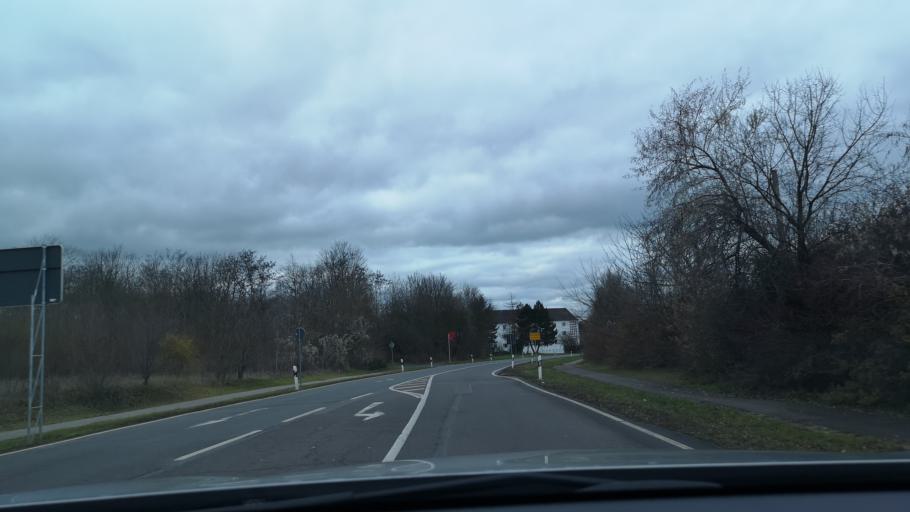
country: DE
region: Saxony-Anhalt
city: Krumpa
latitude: 51.2899
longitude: 11.8573
